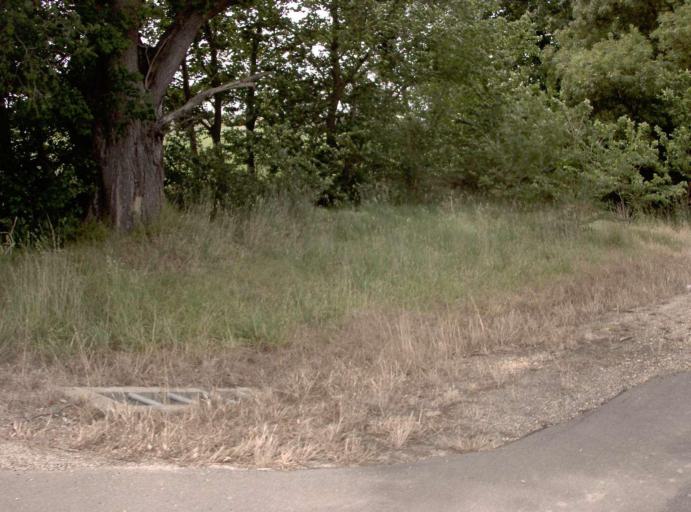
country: AU
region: Victoria
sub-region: Wellington
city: Sale
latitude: -37.9886
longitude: 146.9954
